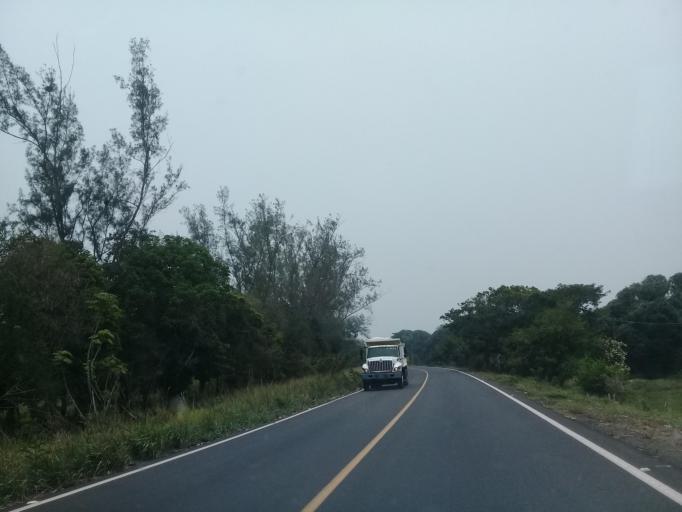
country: MX
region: Veracruz
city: Paso del Toro
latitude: 18.9723
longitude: -96.1798
